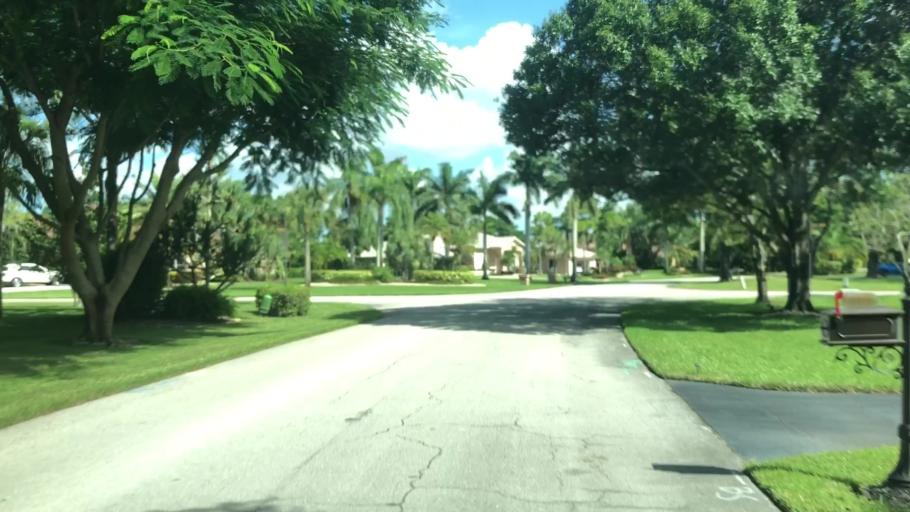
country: US
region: Florida
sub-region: Broward County
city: Parkland
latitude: 26.2900
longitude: -80.2312
